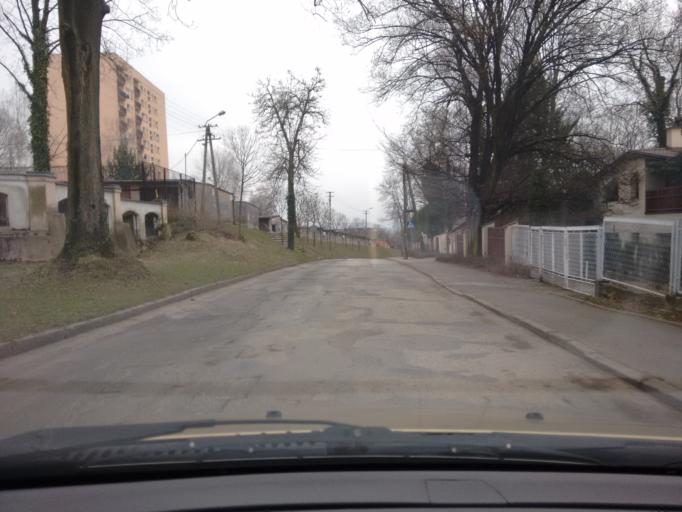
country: PL
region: Silesian Voivodeship
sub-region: Powiat cieszynski
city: Cieszyn
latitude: 49.7573
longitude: 18.6294
